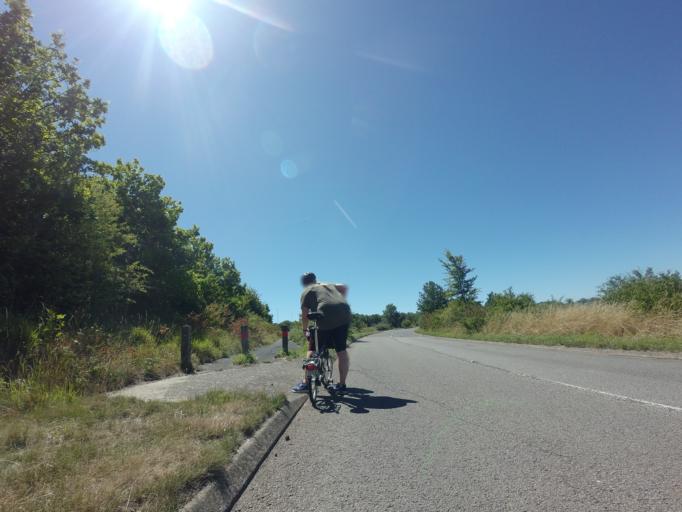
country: GB
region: England
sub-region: Kent
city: Eastry
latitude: 51.2084
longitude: 1.2993
